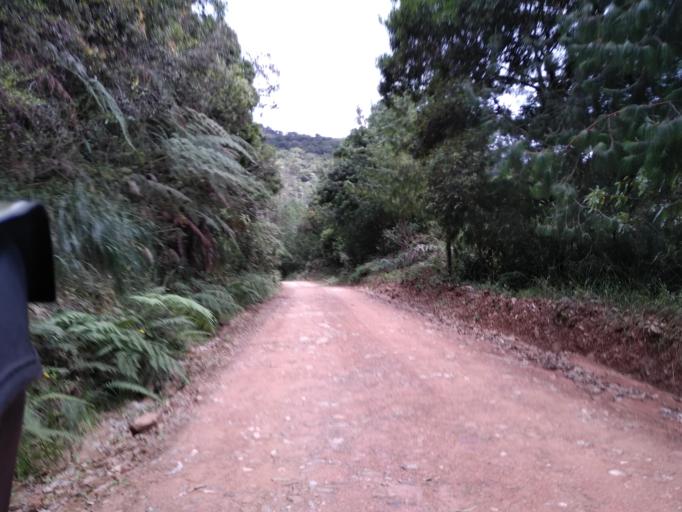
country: CO
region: Boyaca
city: Paipa
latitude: 5.9595
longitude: -73.1650
